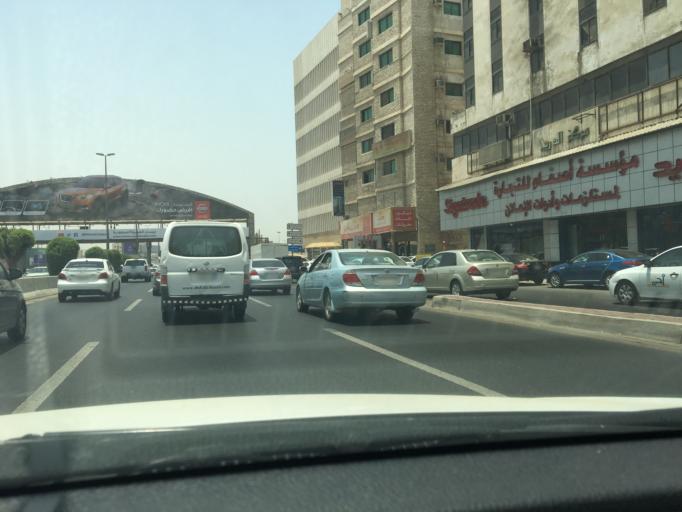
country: SA
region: Makkah
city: Jeddah
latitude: 21.5359
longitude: 39.1922
